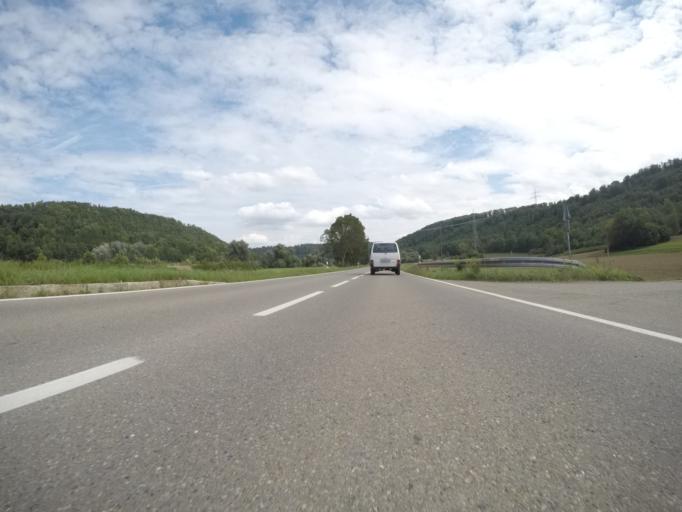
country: DE
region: Baden-Wuerttemberg
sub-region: Tuebingen Region
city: Hirrlingen
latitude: 48.4589
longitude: 8.8829
